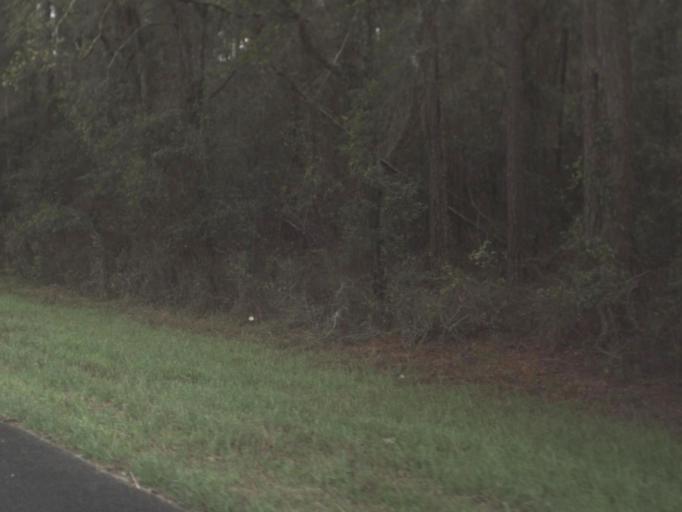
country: US
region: Florida
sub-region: Gadsden County
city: Havana
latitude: 30.5422
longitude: -84.3723
